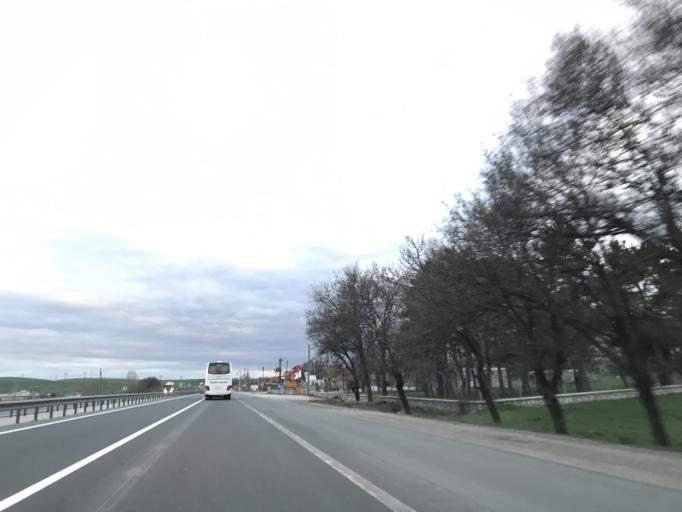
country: TR
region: Ankara
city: Ikizce
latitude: 39.4857
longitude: 32.8698
